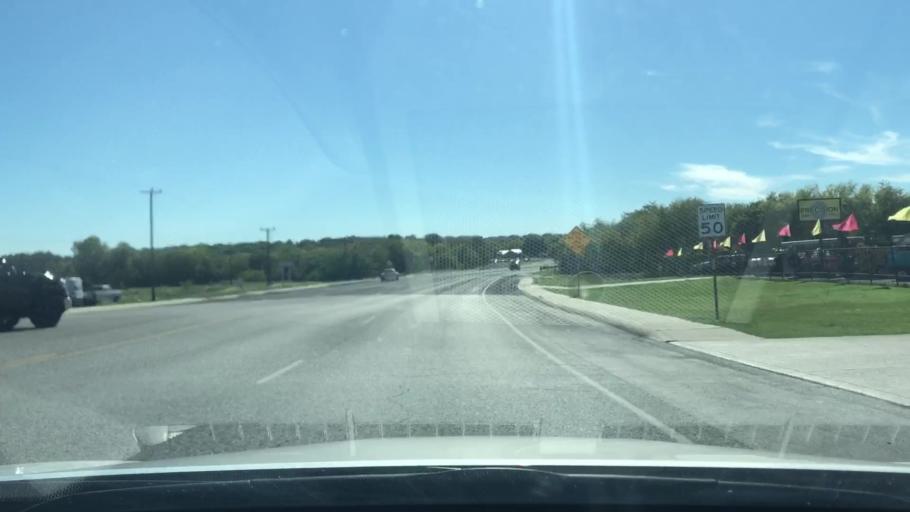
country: US
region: Texas
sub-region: Bexar County
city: Converse
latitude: 29.5072
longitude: -98.3096
